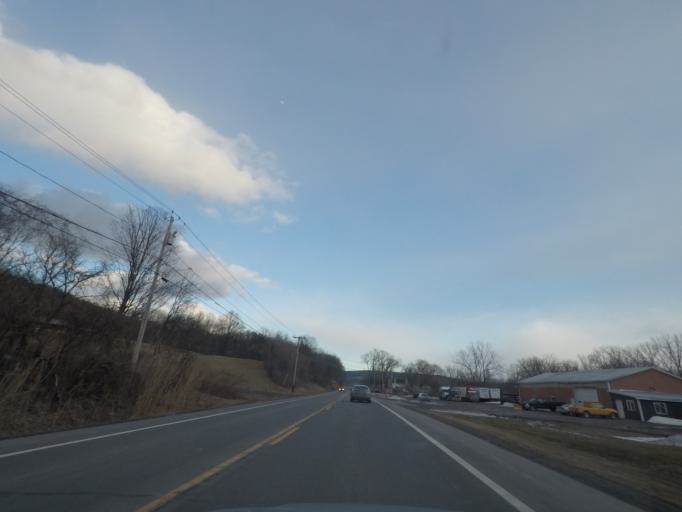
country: US
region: New York
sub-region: Herkimer County
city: Ilion
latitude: 43.0260
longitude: -75.0388
